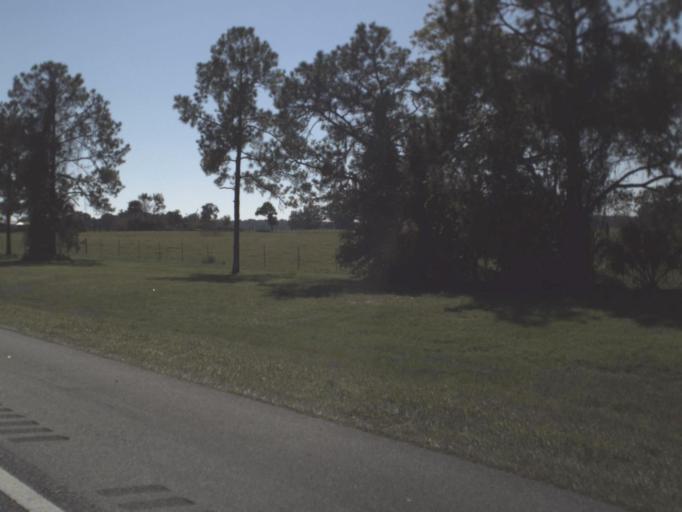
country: US
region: Florida
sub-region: Sumter County
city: Wildwood
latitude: 28.7949
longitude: -81.9943
